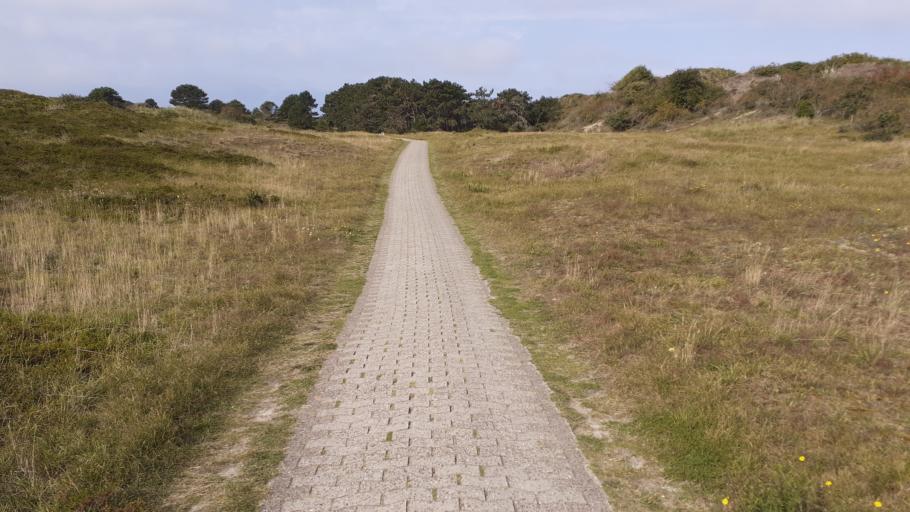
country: DE
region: Lower Saxony
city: Spiekeroog
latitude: 53.7778
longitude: 7.7045
